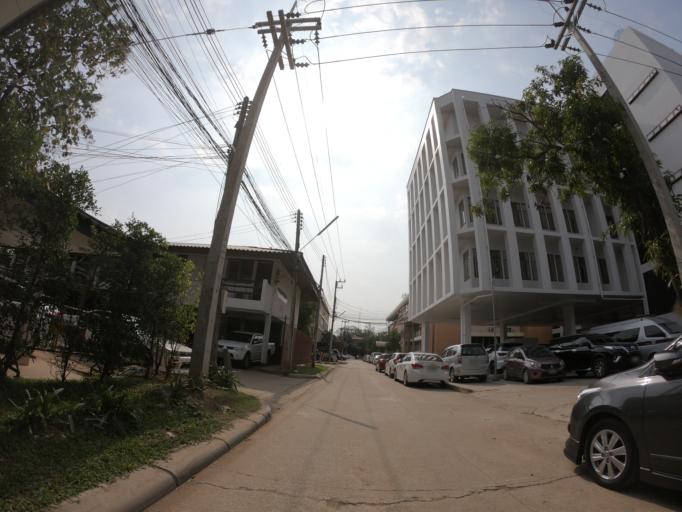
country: TH
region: Chiang Mai
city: Chiang Mai
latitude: 18.7603
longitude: 98.9997
